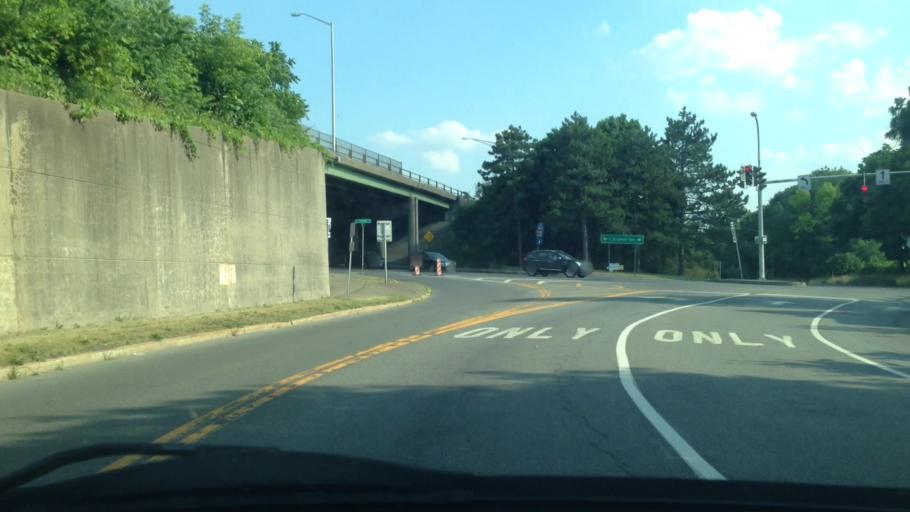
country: US
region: New York
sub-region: Onondaga County
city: Syracuse
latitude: 43.0209
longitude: -76.1410
